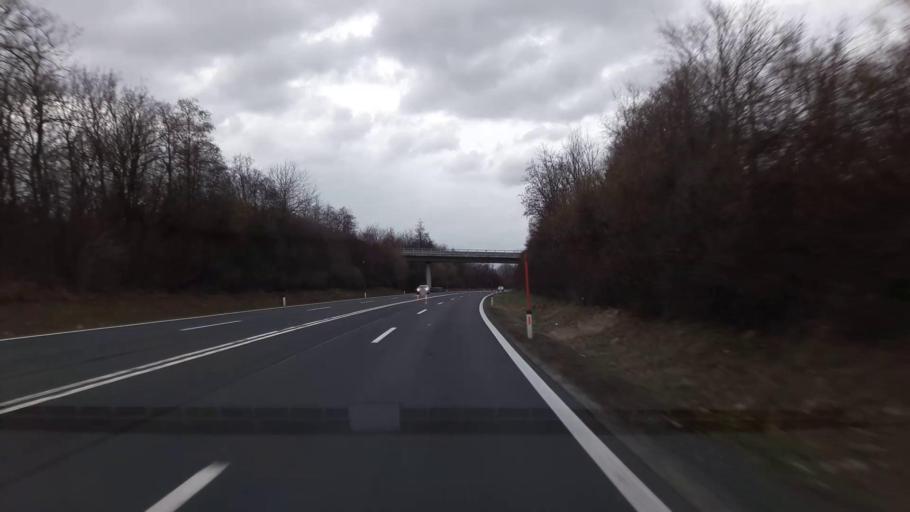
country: AT
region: Burgenland
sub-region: Politischer Bezirk Mattersburg
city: Mattersburg
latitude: 47.7288
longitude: 16.3732
